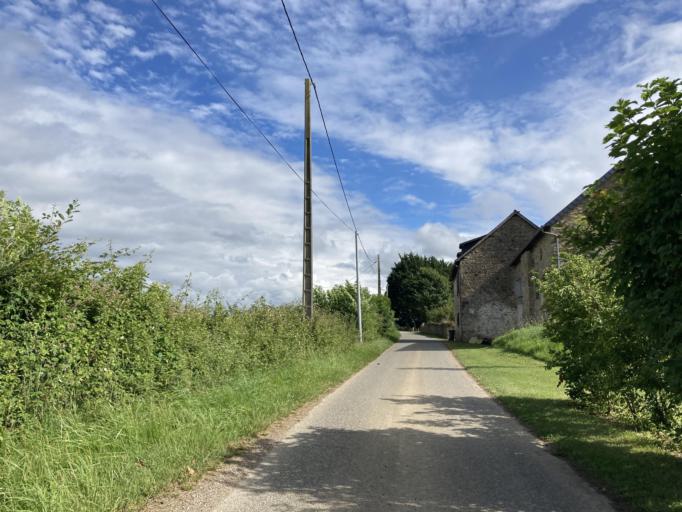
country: FR
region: Aquitaine
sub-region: Departement des Pyrenees-Atlantiques
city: Ledeuix
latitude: 43.2545
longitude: -0.6246
